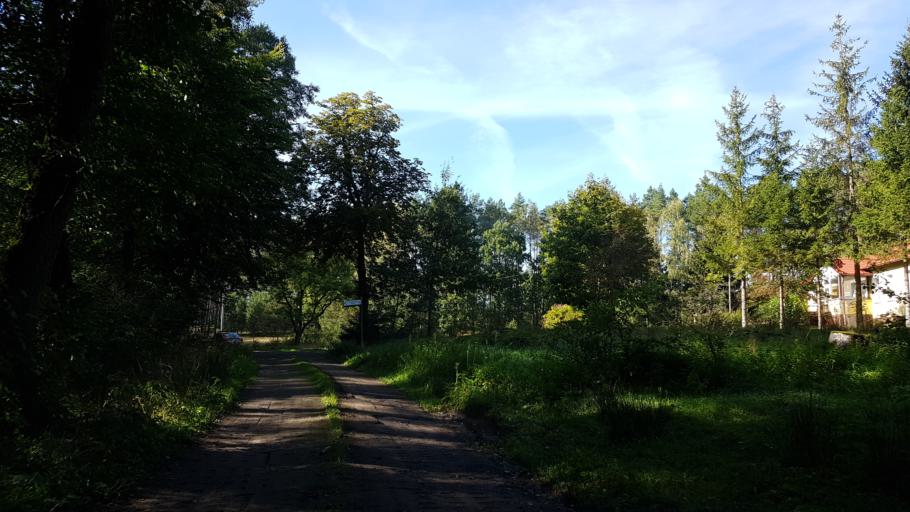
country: PL
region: West Pomeranian Voivodeship
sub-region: Powiat koszalinski
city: Bobolice
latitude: 54.0540
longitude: 16.5951
